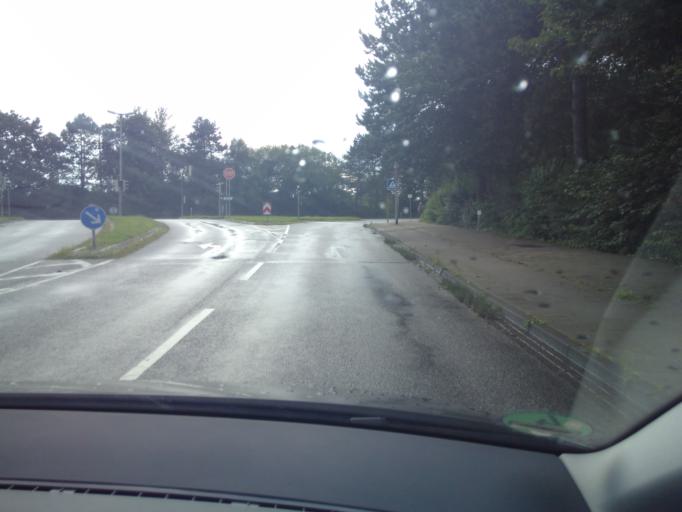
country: DE
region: Lower Saxony
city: Cuxhaven
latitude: 53.8742
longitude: 8.6799
